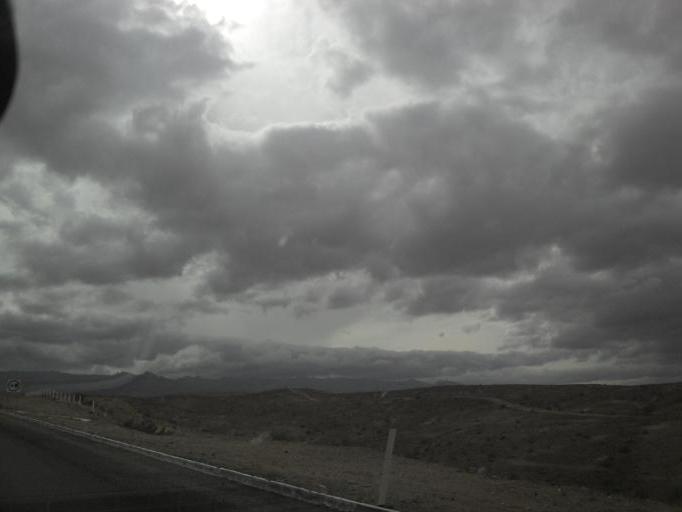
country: MX
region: Baja California
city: Progreso
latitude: 32.5654
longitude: -115.8624
